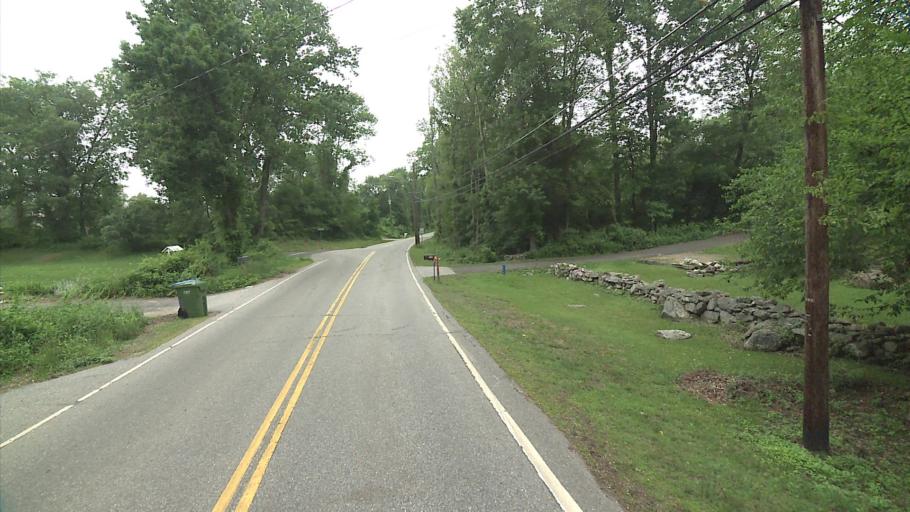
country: US
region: Connecticut
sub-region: Tolland County
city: Hebron
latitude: 41.6921
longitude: -72.3615
